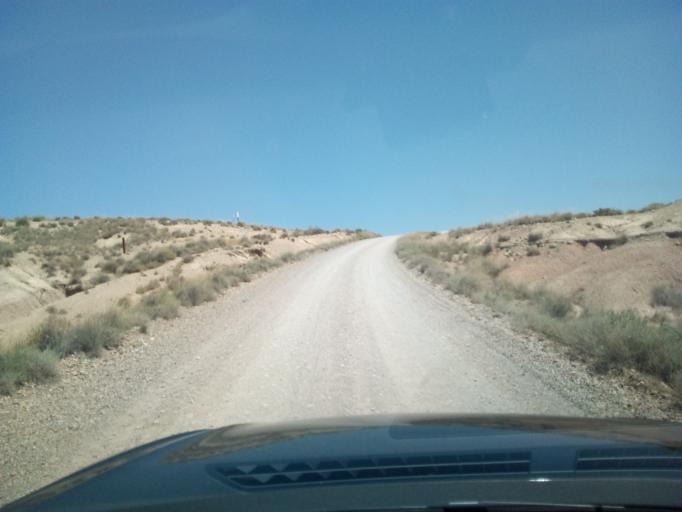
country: ES
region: Navarre
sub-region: Provincia de Navarra
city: Fustinana
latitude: 42.1669
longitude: -1.4266
